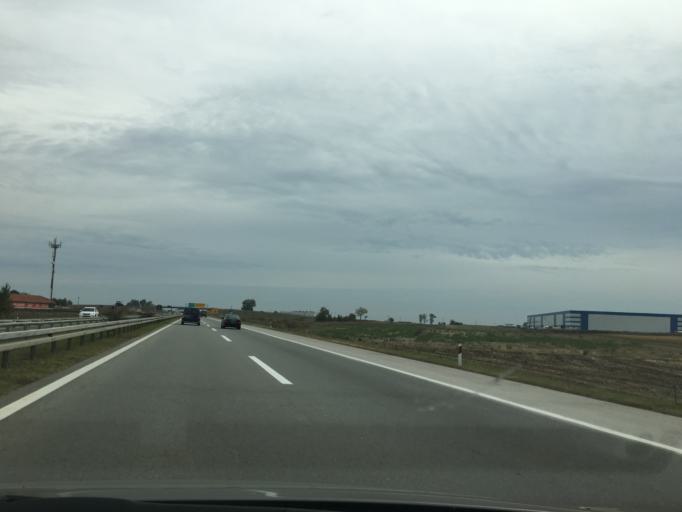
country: RS
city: Novi Banovci
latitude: 44.9469
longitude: 20.2754
